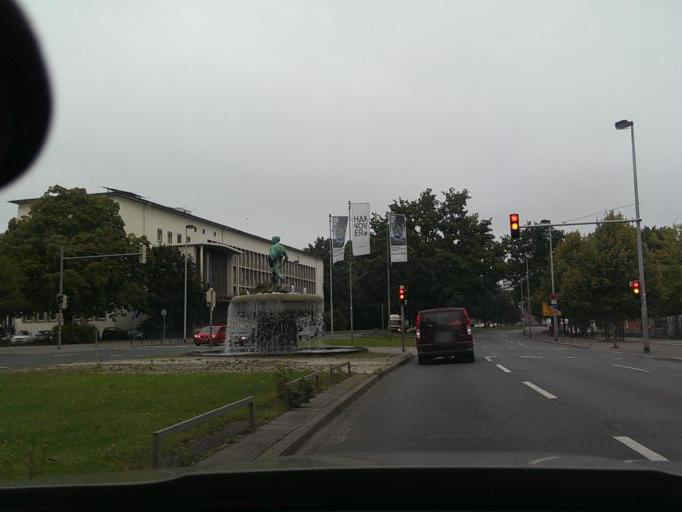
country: DE
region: Lower Saxony
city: Hannover
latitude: 52.3706
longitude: 9.7310
